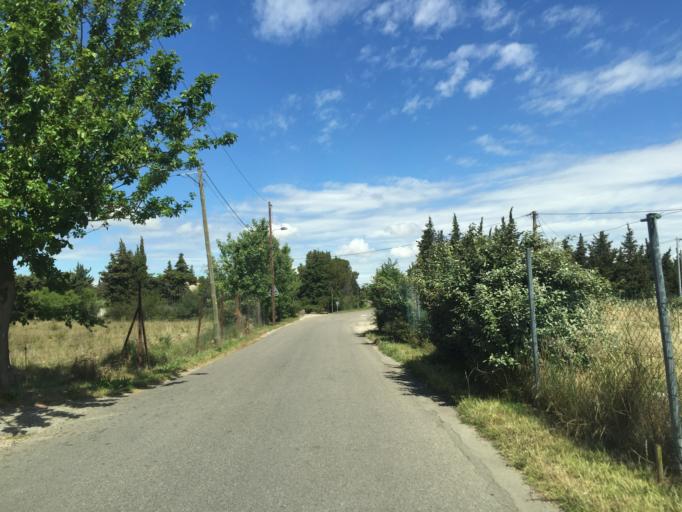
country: FR
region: Provence-Alpes-Cote d'Azur
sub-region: Departement du Vaucluse
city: Sorgues
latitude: 43.9972
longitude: 4.8909
